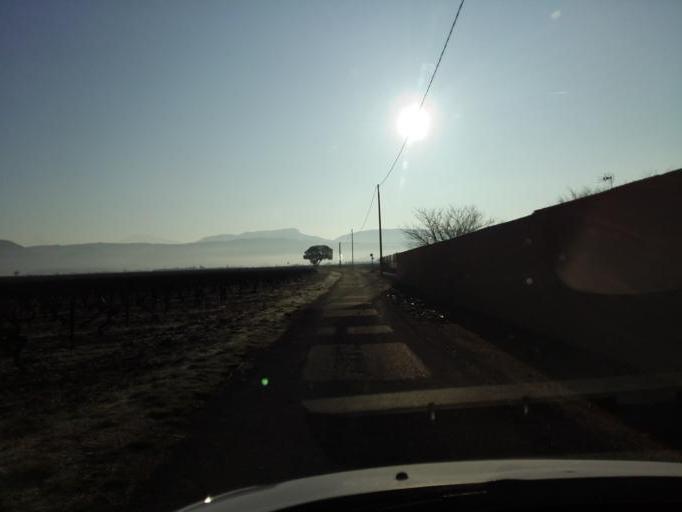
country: FR
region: Provence-Alpes-Cote d'Azur
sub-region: Departement du Vaucluse
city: Sablet
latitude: 44.2095
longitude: 4.9685
